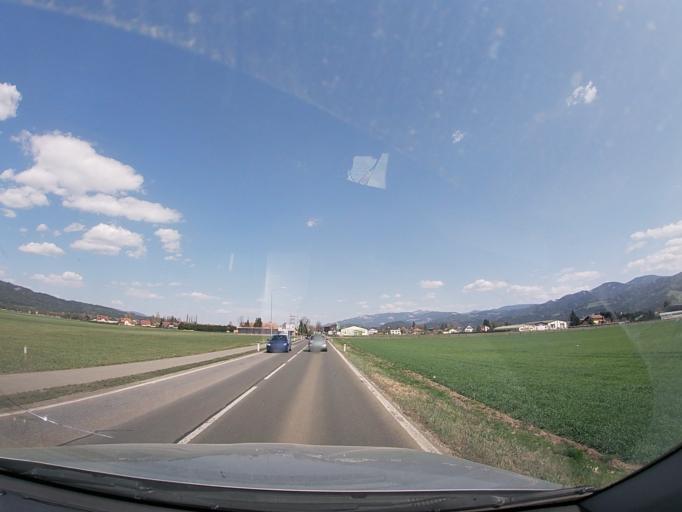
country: AT
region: Styria
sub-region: Politischer Bezirk Murtal
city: Spielberg bei Knittelfeld
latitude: 47.2029
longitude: 14.7876
